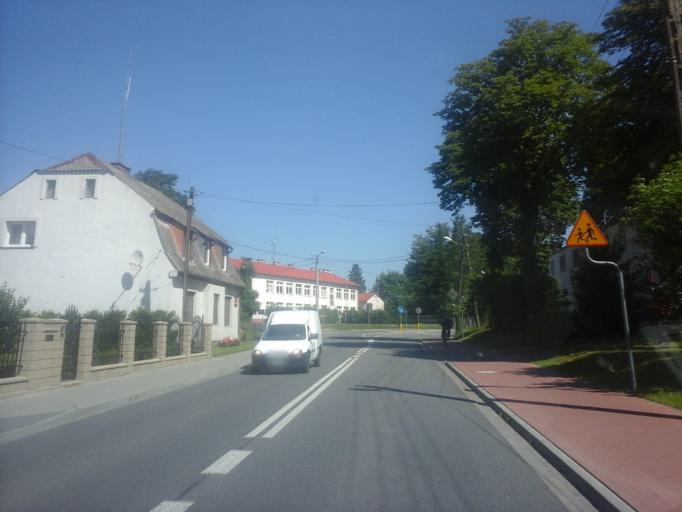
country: PL
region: West Pomeranian Voivodeship
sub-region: Koszalin
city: Koszalin
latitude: 54.1225
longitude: 16.1681
